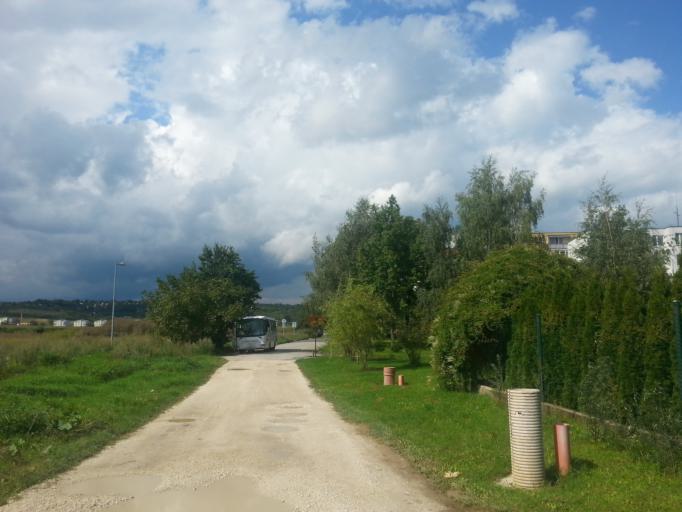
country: SK
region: Trenciansky
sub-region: Okres Nove Mesto nad Vahom
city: Nove Mesto nad Vahom
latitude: 48.7503
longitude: 17.8206
